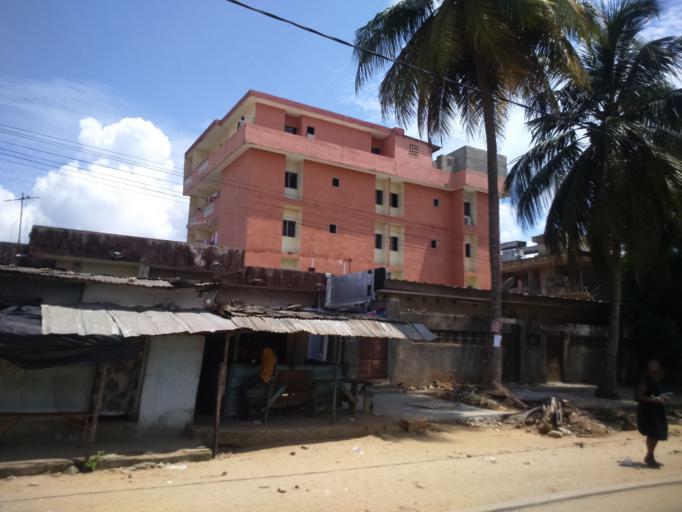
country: CI
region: Lagunes
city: Abidjan
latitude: 5.3450
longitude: -4.0875
